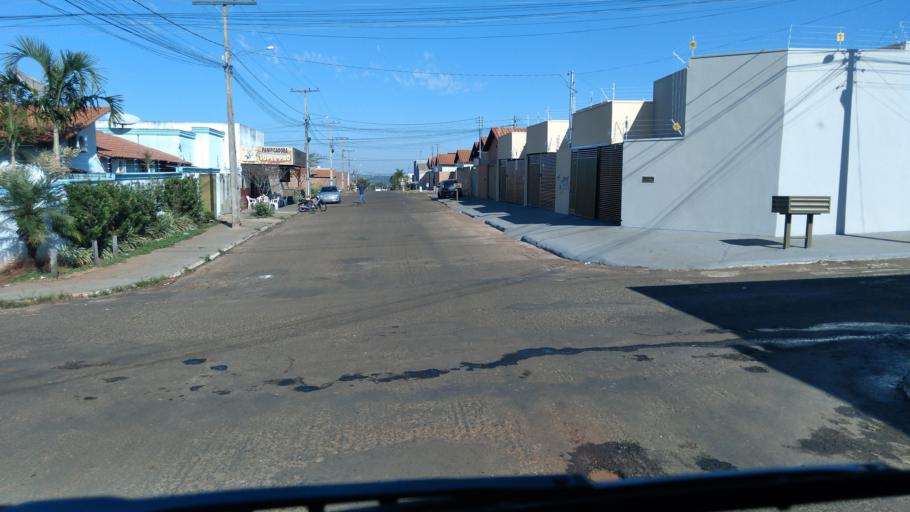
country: BR
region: Goias
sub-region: Mineiros
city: Mineiros
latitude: -17.5730
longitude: -52.5740
